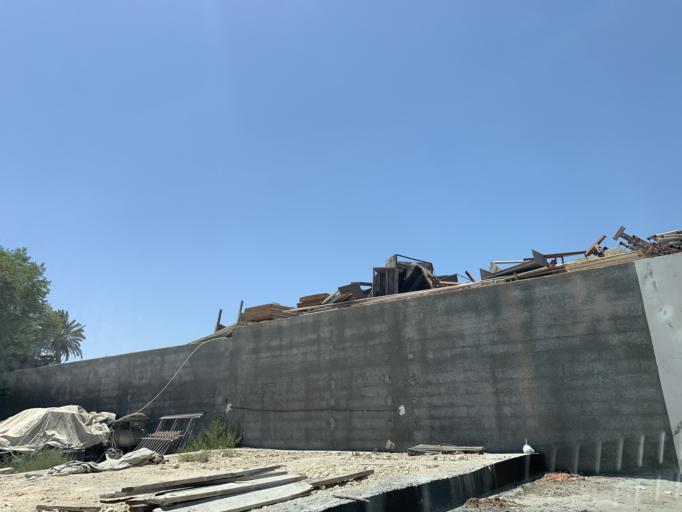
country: BH
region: Manama
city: Jidd Hafs
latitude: 26.2268
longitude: 50.4939
